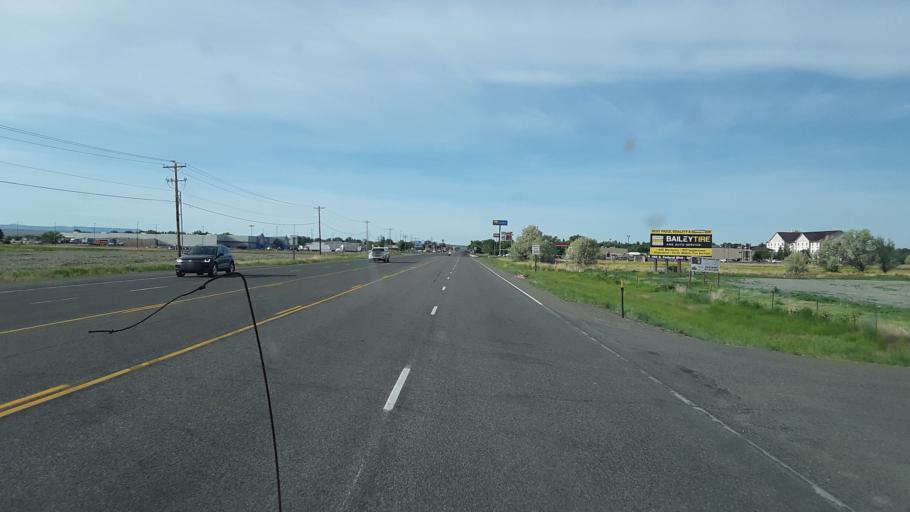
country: US
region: Wyoming
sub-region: Fremont County
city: Riverton
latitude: 43.0479
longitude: -108.3808
